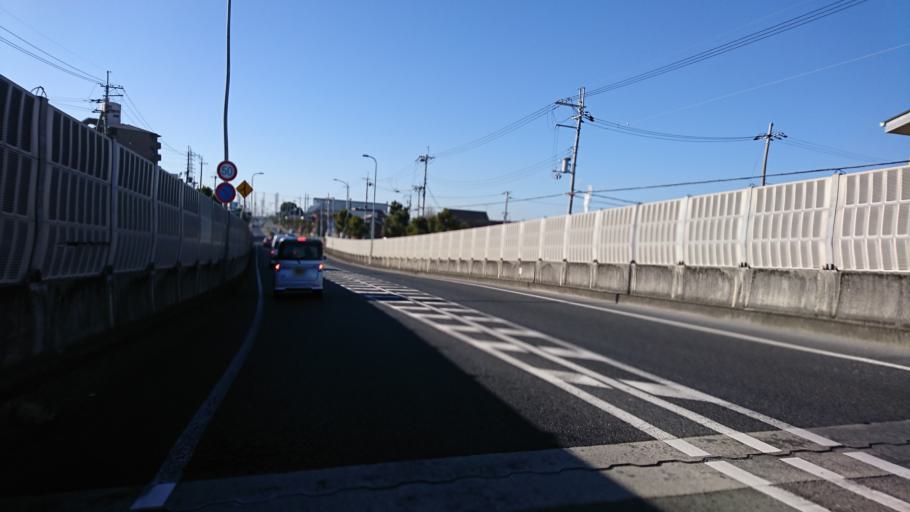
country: JP
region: Hyogo
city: Kakogawacho-honmachi
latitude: 34.7808
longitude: 134.8147
